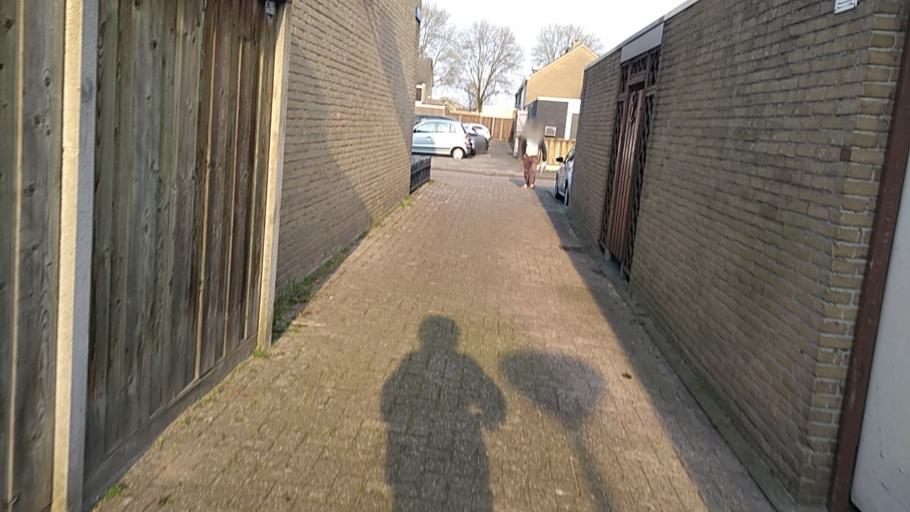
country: NL
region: Overijssel
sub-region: Gemeente Almelo
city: Almelo
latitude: 52.3824
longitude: 6.6745
